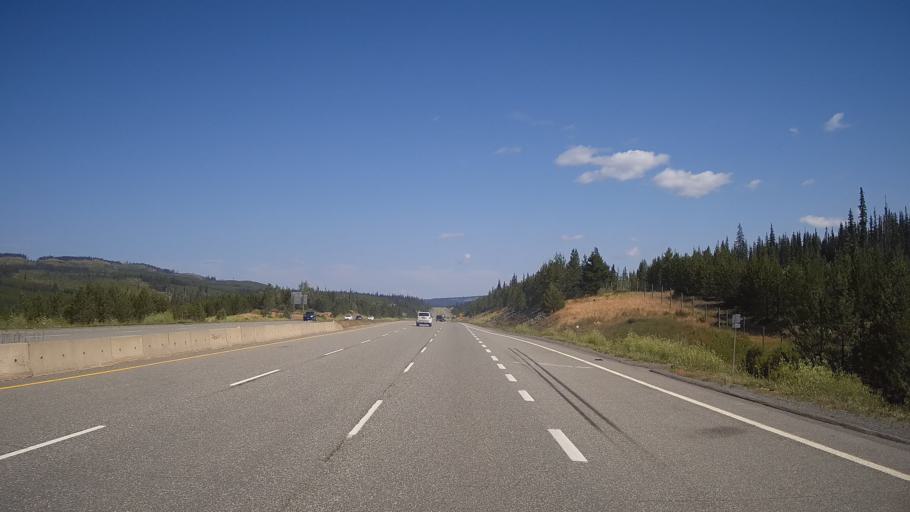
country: CA
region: British Columbia
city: Logan Lake
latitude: 50.3237
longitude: -120.6361
